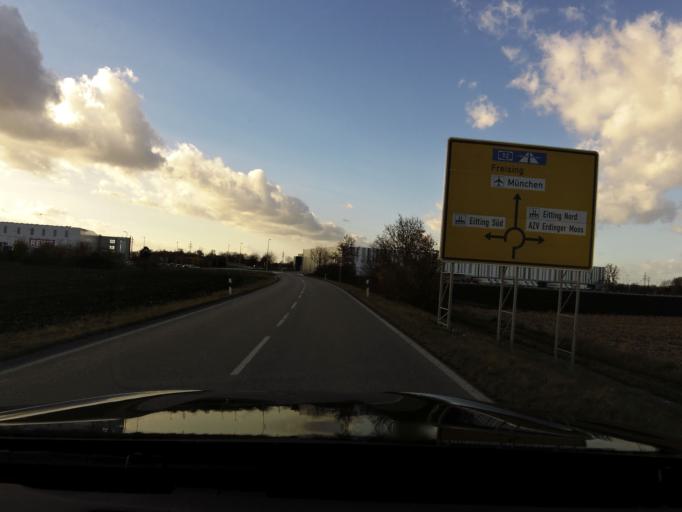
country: DE
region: Bavaria
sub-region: Upper Bavaria
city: Eitting
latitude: 48.3712
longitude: 11.8940
